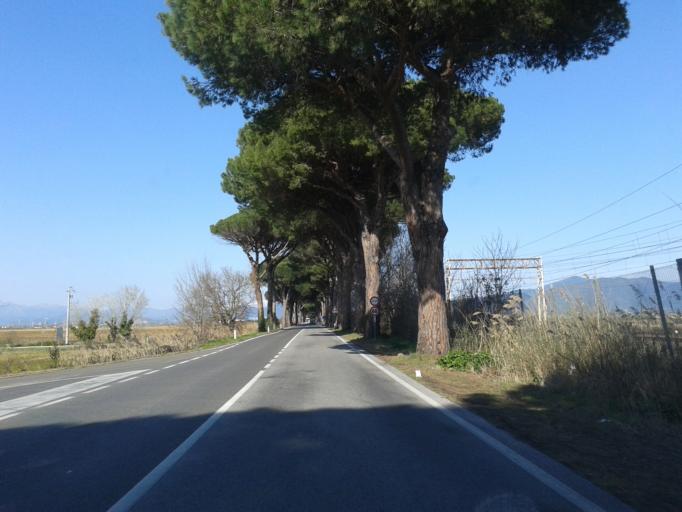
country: IT
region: Tuscany
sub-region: Province of Pisa
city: Pisa
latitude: 43.6649
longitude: 10.3710
